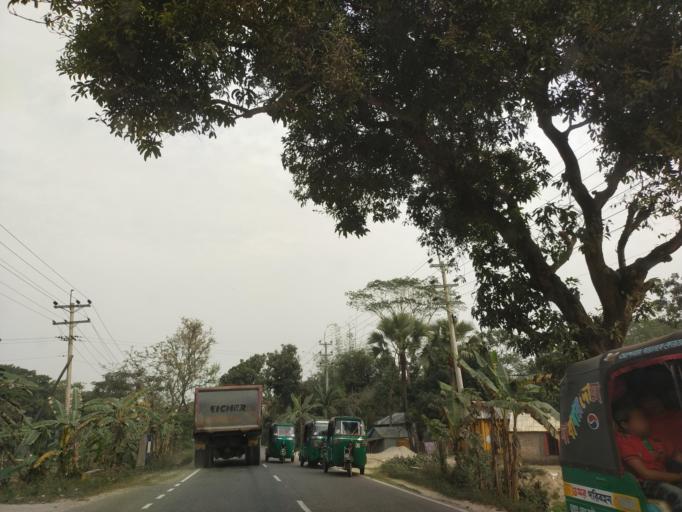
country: BD
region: Dhaka
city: Narsingdi
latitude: 24.0255
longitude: 90.7384
